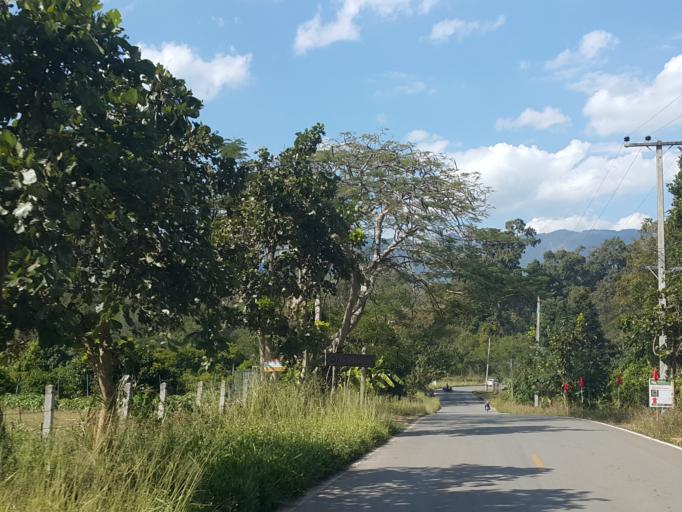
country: TH
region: Chiang Mai
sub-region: Amphoe Chiang Dao
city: Chiang Dao
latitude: 19.3784
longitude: 98.9443
